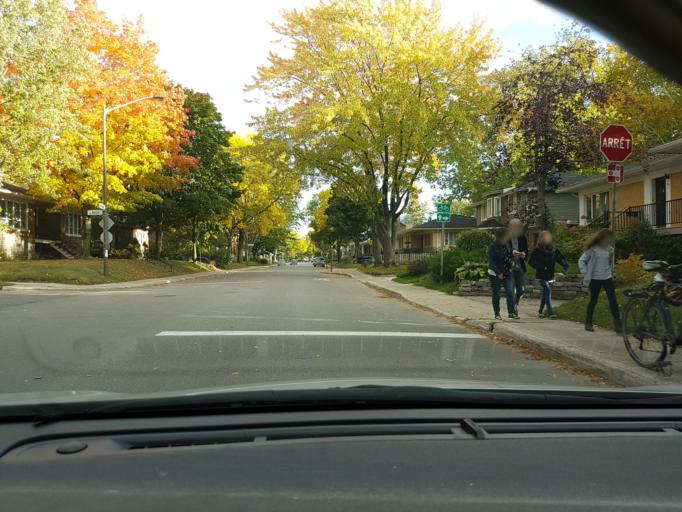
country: CA
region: Quebec
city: Quebec
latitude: 46.7919
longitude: -71.2568
